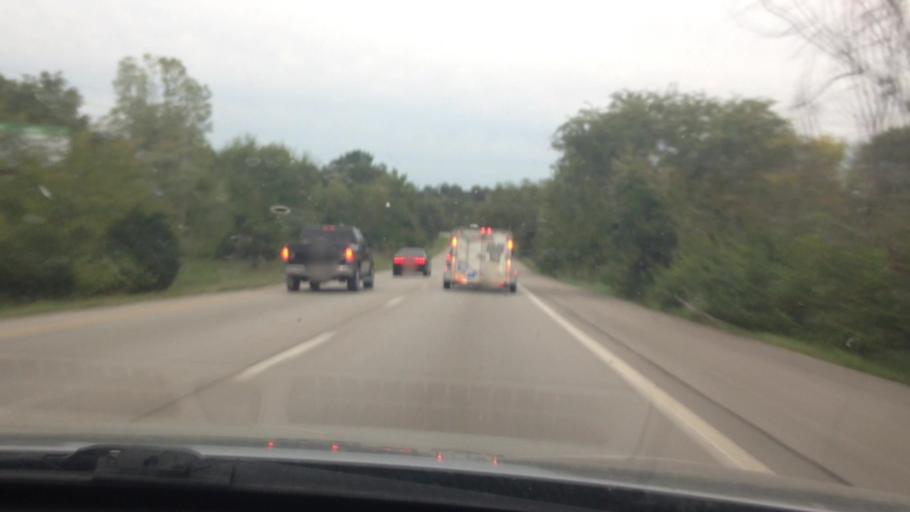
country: US
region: Missouri
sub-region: Jackson County
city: Raytown
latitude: 38.9708
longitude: -94.4414
